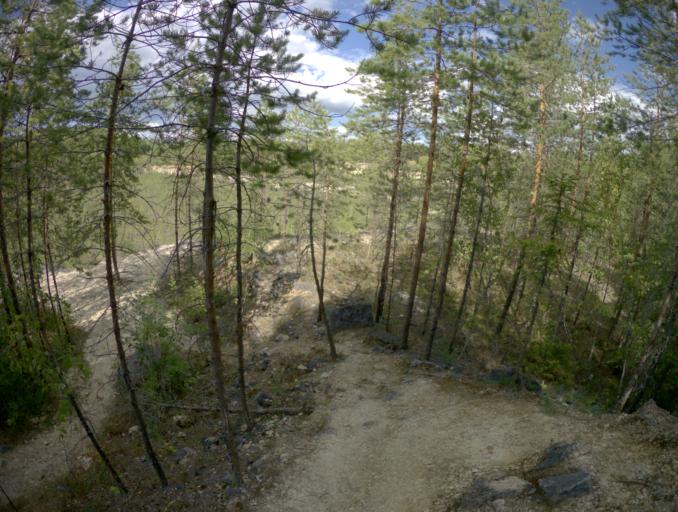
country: RU
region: Vladimir
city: Krasnyy Bogatyr'
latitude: 56.0095
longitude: 41.0636
